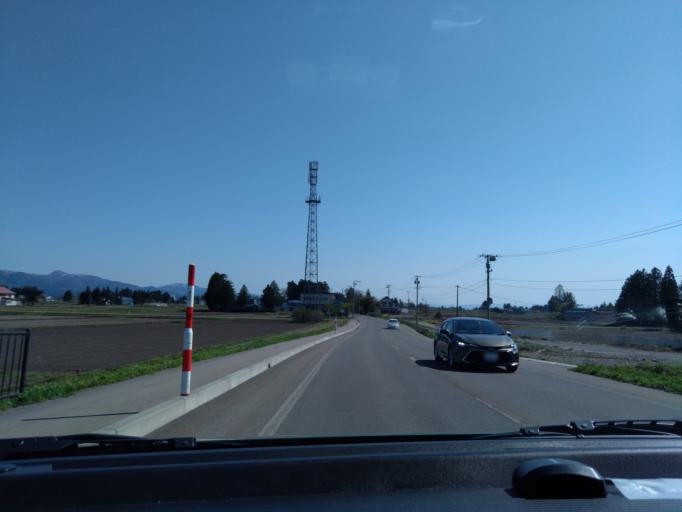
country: JP
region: Akita
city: Kakunodatemachi
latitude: 39.5426
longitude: 140.5856
